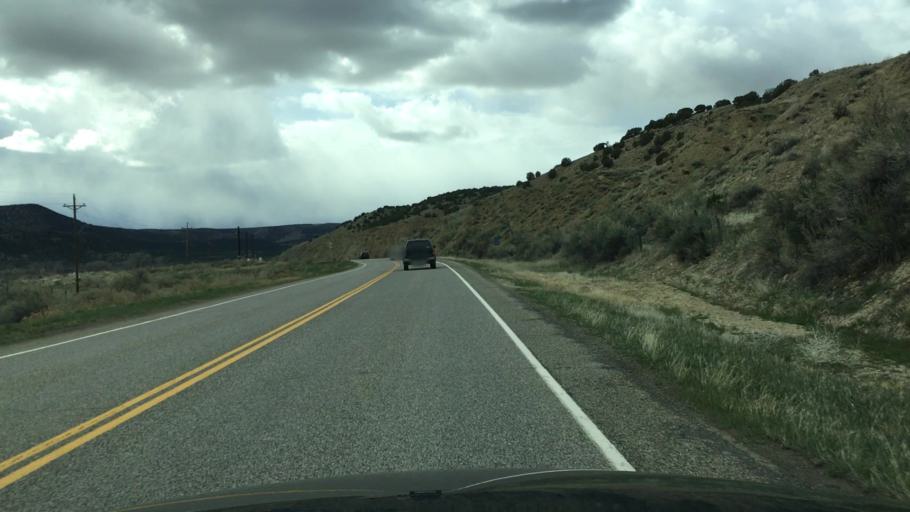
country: US
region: Colorado
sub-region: Rio Blanco County
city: Meeker
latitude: 40.0949
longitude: -108.2188
